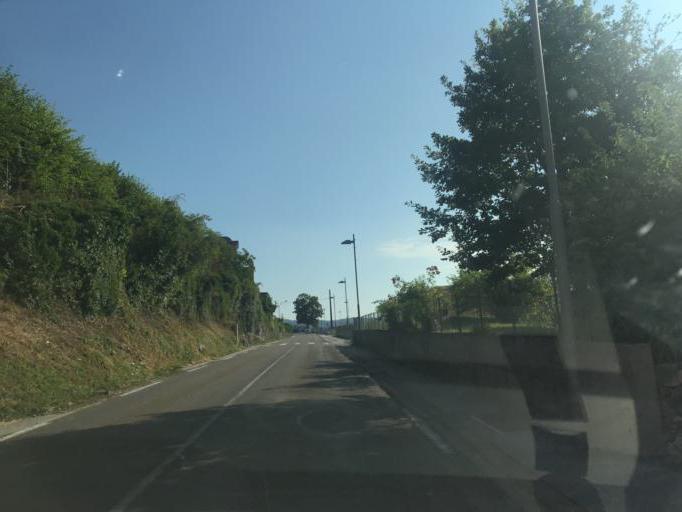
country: FR
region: Franche-Comte
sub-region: Departement du Jura
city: Lavans-les-Saint-Claude
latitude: 46.3842
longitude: 5.7783
